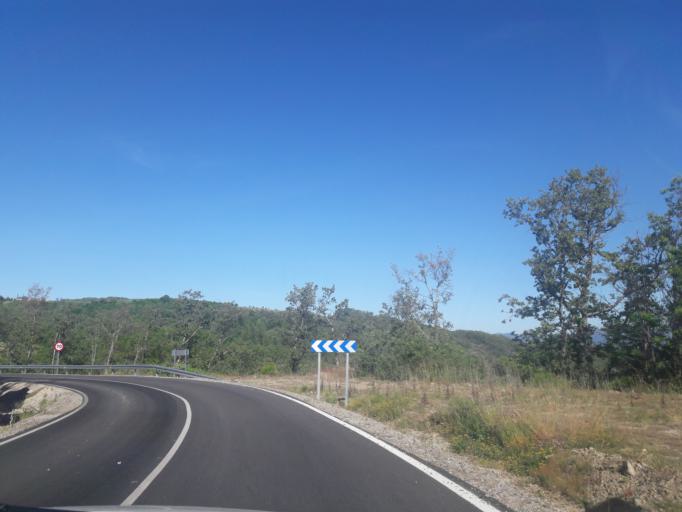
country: ES
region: Castille and Leon
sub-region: Provincia de Salamanca
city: Montemayor del Rio
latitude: 40.3351
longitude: -5.9002
